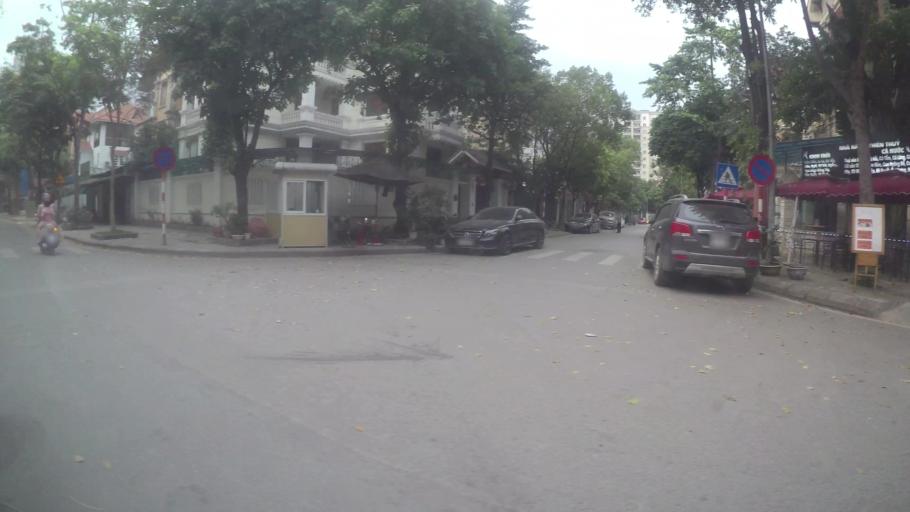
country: VN
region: Ha Noi
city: Cau Dien
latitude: 21.0315
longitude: 105.7681
